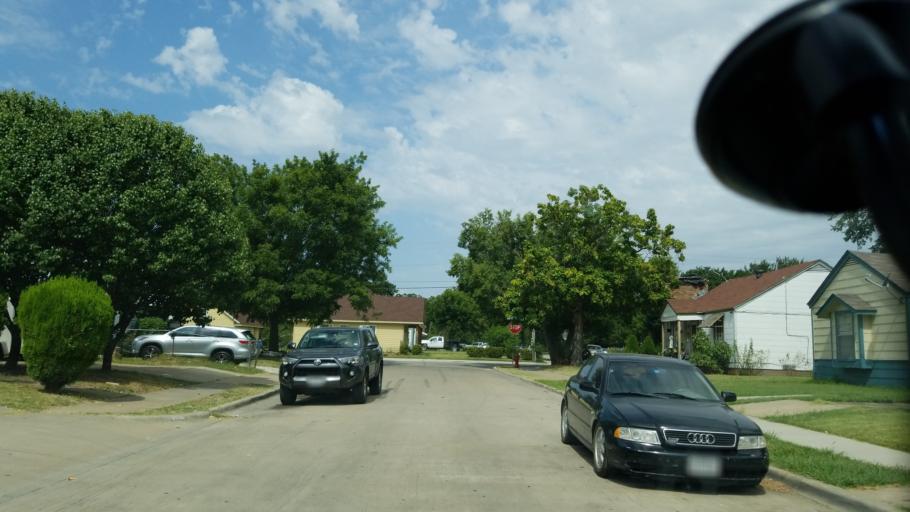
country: US
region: Texas
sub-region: Dallas County
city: Grand Prairie
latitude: 32.7504
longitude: -96.9855
